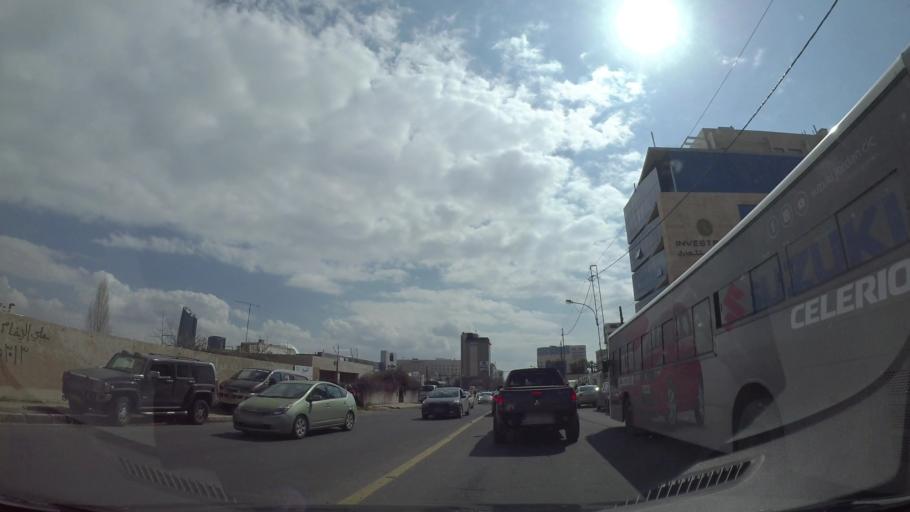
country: JO
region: Amman
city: Amman
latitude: 31.9721
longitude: 35.8968
